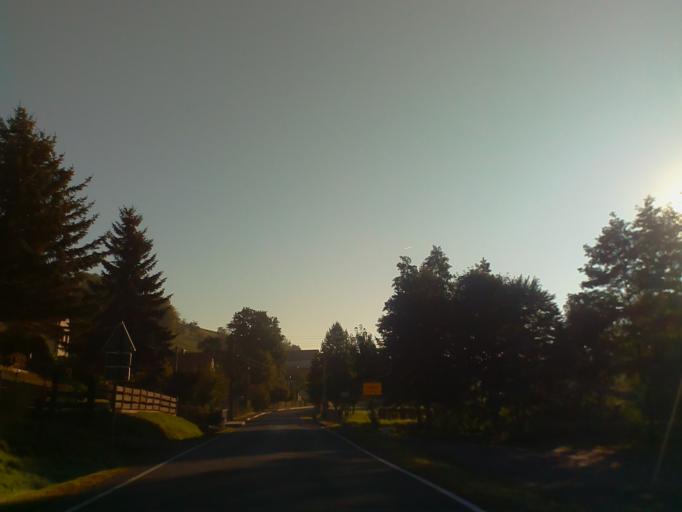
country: DE
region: Thuringia
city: Kleinebersdorf
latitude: 50.8304
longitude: 11.8449
